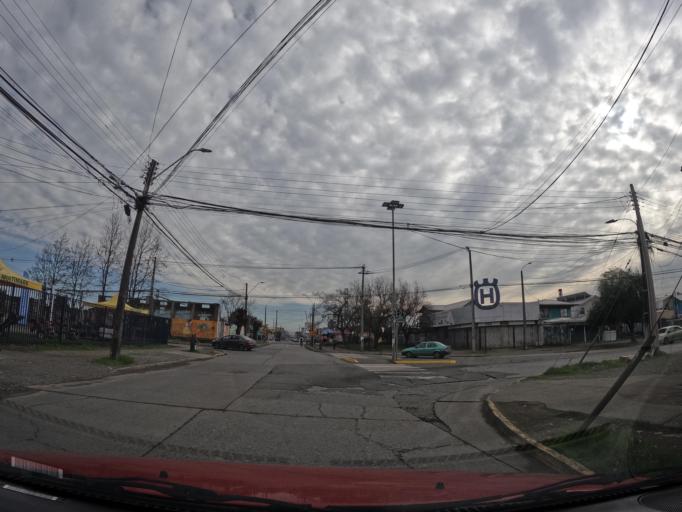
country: CL
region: Maule
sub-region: Provincia de Linares
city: Linares
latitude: -35.8490
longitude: -71.5900
